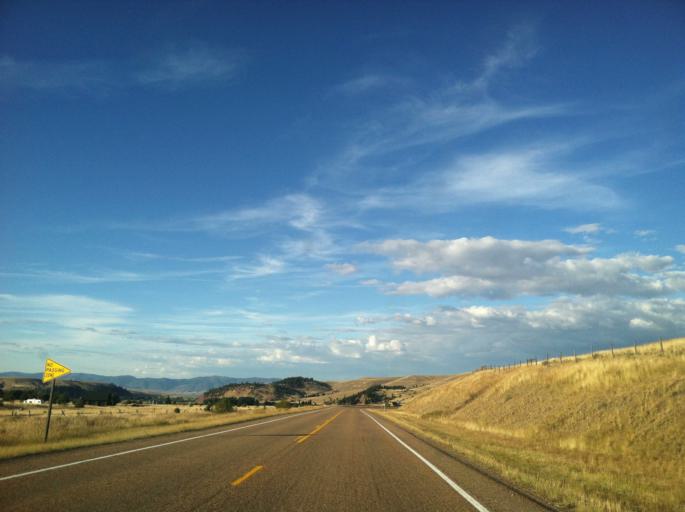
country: US
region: Montana
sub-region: Granite County
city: Philipsburg
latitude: 46.4867
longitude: -113.2315
